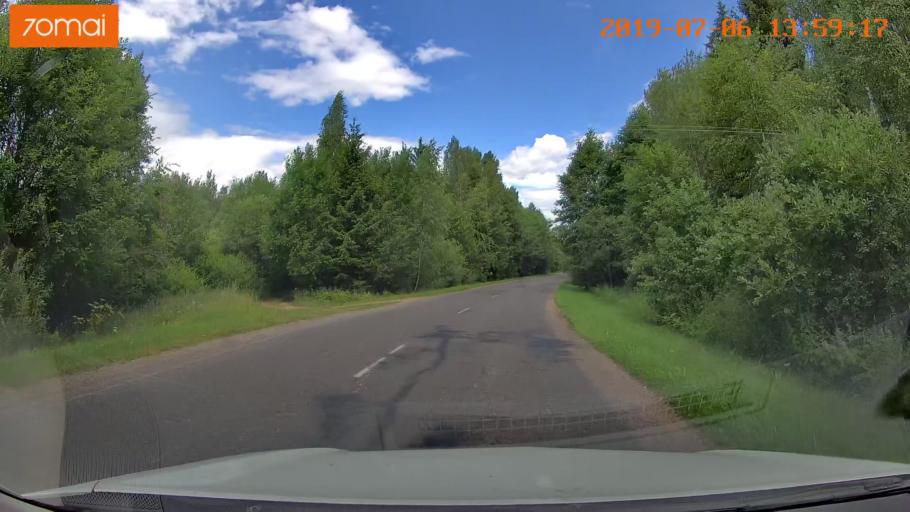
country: BY
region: Minsk
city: Ivyanyets
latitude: 53.7932
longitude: 26.8125
